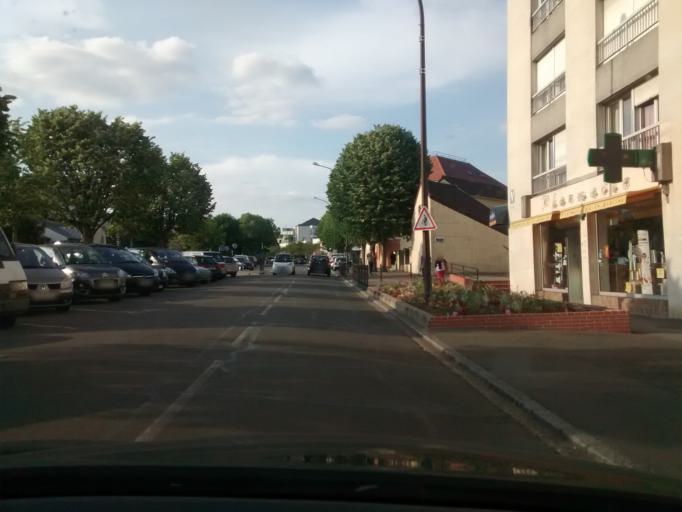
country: FR
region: Ile-de-France
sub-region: Departement des Yvelines
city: Le Chesnay
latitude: 48.8248
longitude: 2.1258
